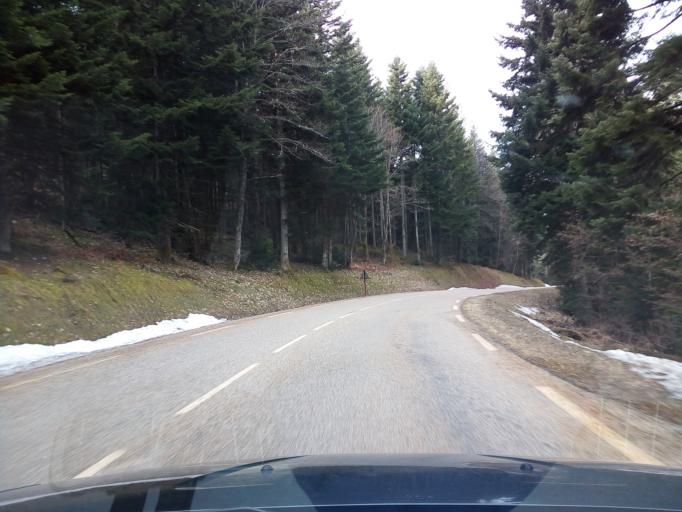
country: FR
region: Rhone-Alpes
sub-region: Departement de l'Isere
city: Revel
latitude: 45.1520
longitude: 5.8857
